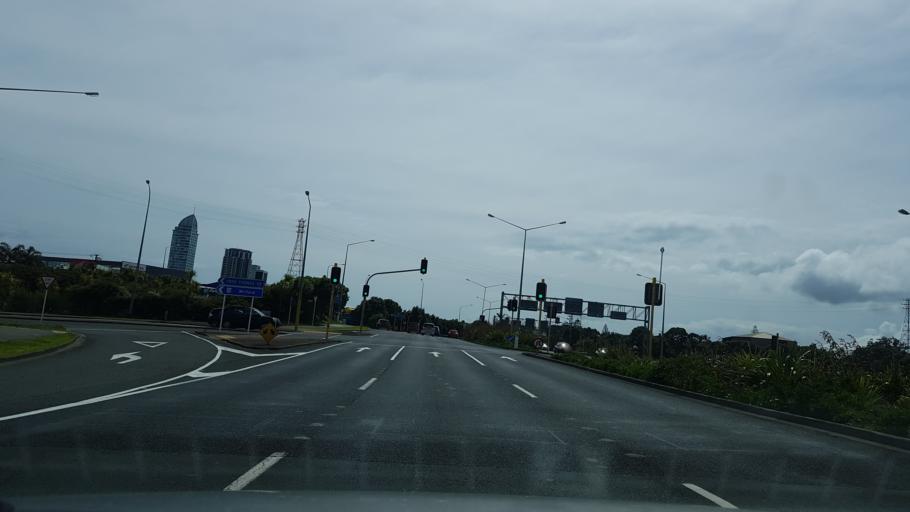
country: NZ
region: Auckland
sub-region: Auckland
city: North Shore
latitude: -36.7972
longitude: 174.7646
